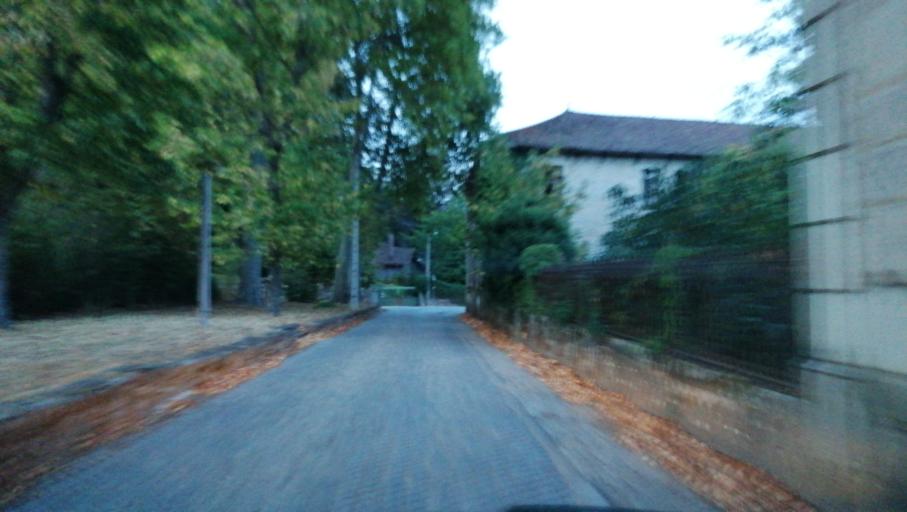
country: PT
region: Vila Real
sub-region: Vila Pouca de Aguiar
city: Vila Pouca de Aguiar
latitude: 41.5436
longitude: -7.6081
